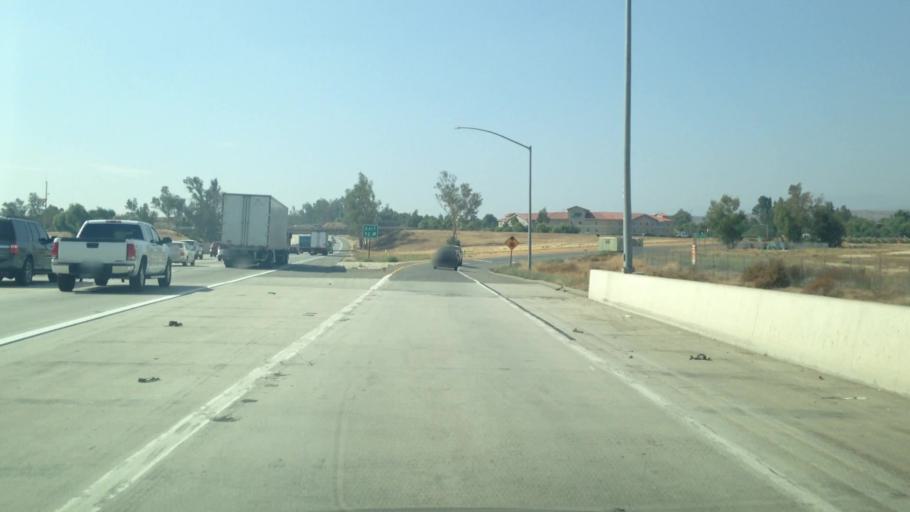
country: US
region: California
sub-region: Riverside County
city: Beaumont
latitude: 33.9426
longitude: -117.0008
